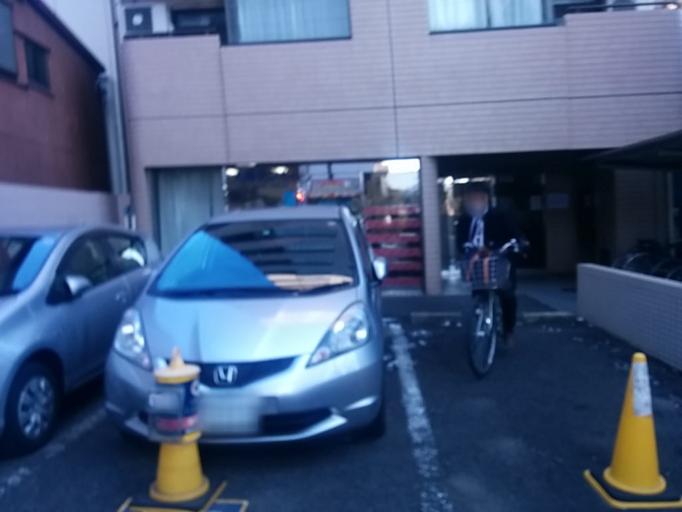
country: JP
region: Tokyo
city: Tokyo
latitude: 35.7274
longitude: 139.7526
